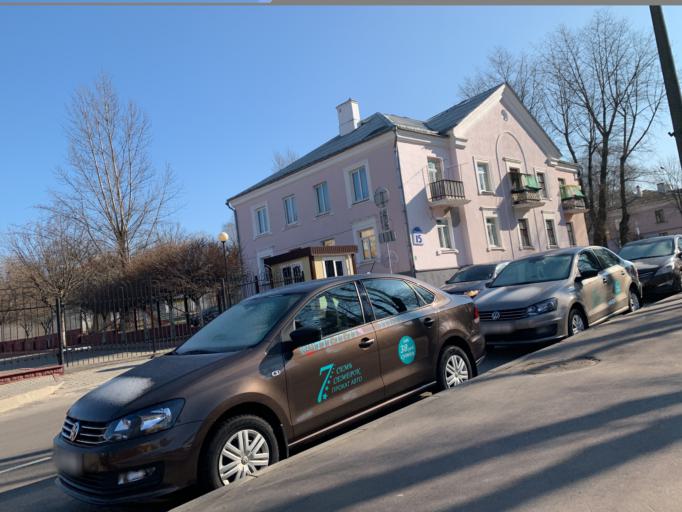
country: BY
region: Minsk
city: Minsk
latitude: 53.9097
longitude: 27.5858
